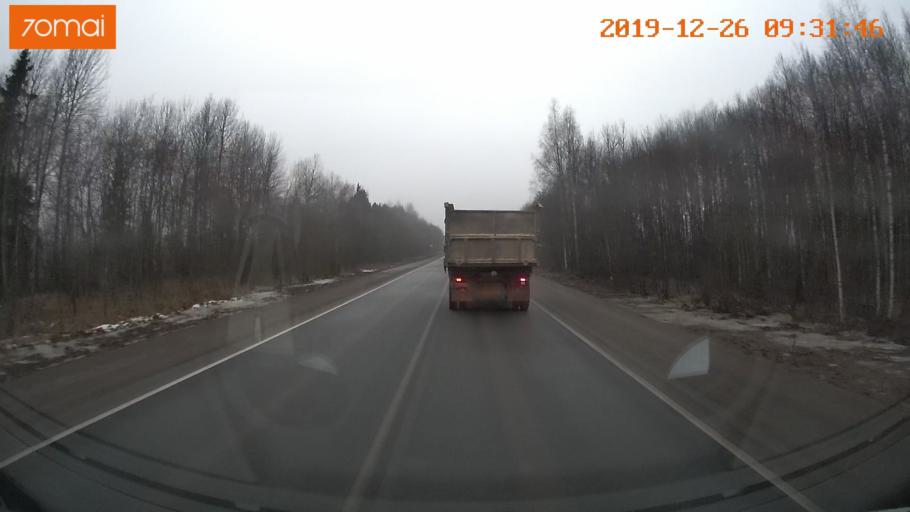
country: RU
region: Vologda
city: Gryazovets
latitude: 59.0719
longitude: 40.1243
